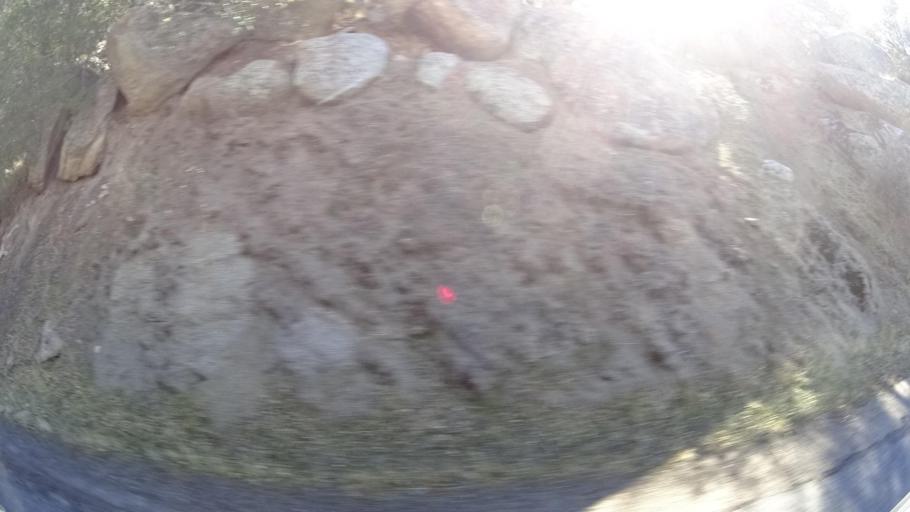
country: US
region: California
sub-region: Kern County
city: Bodfish
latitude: 35.5740
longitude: -118.5585
